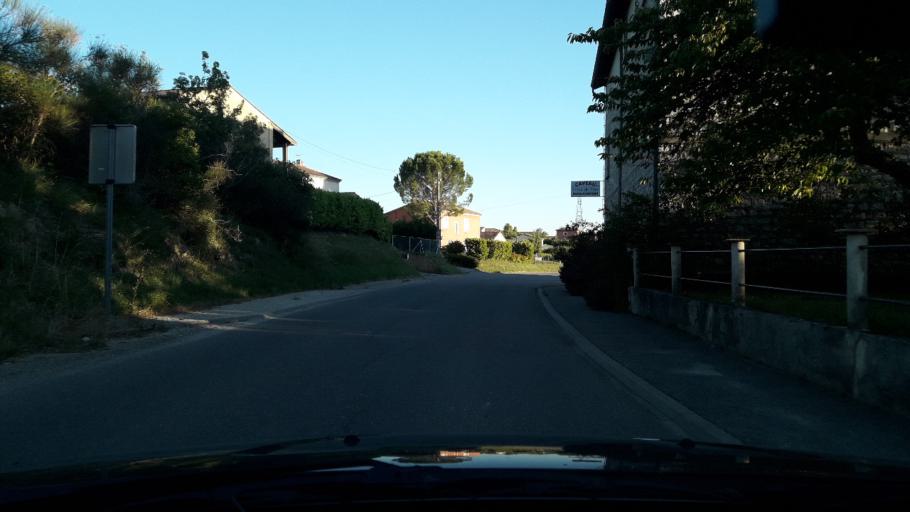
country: FR
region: Rhone-Alpes
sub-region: Departement de l'Ardeche
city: Lavilledieu
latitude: 44.6095
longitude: 4.4732
